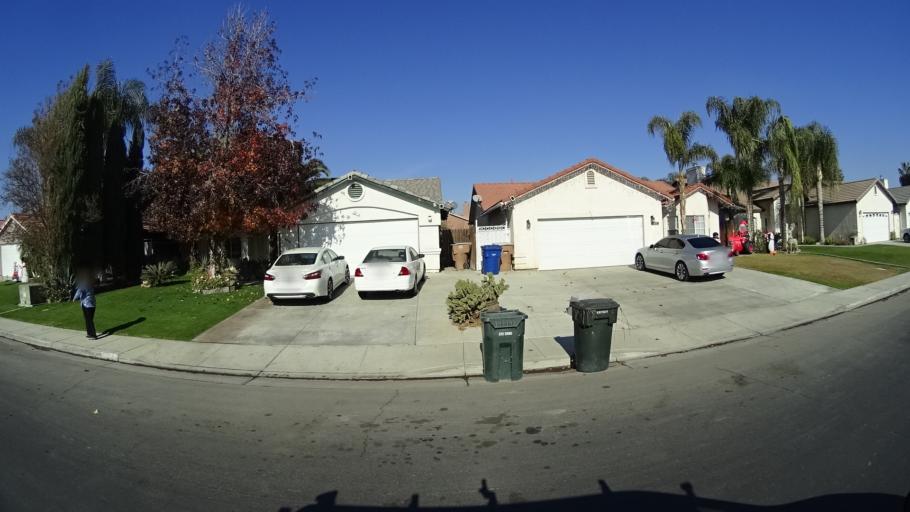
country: US
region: California
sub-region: Kern County
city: Greenfield
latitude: 35.2907
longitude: -119.0467
